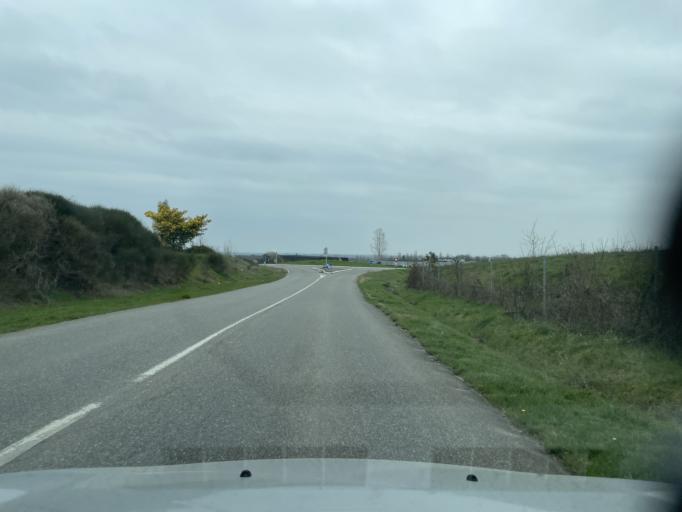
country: FR
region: Midi-Pyrenees
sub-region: Departement du Gers
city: Pujaudran
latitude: 43.5899
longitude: 1.1695
